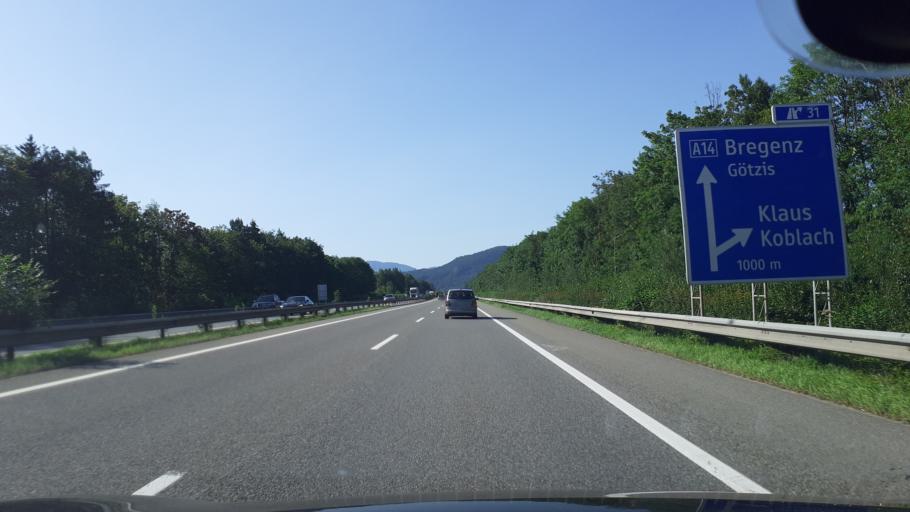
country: AT
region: Vorarlberg
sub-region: Politischer Bezirk Feldkirch
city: Klaus
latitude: 47.2990
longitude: 9.6246
